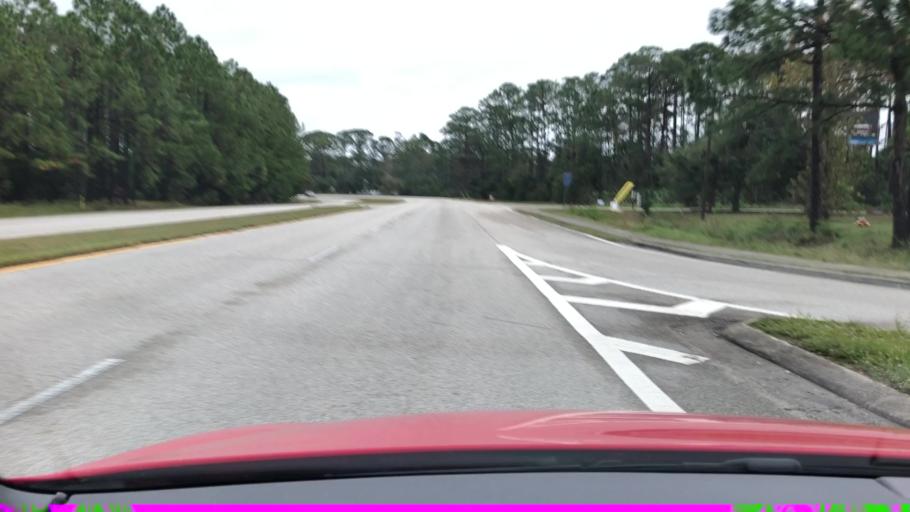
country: US
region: Florida
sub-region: Volusia County
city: Holly Hill
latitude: 29.2094
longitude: -81.0740
